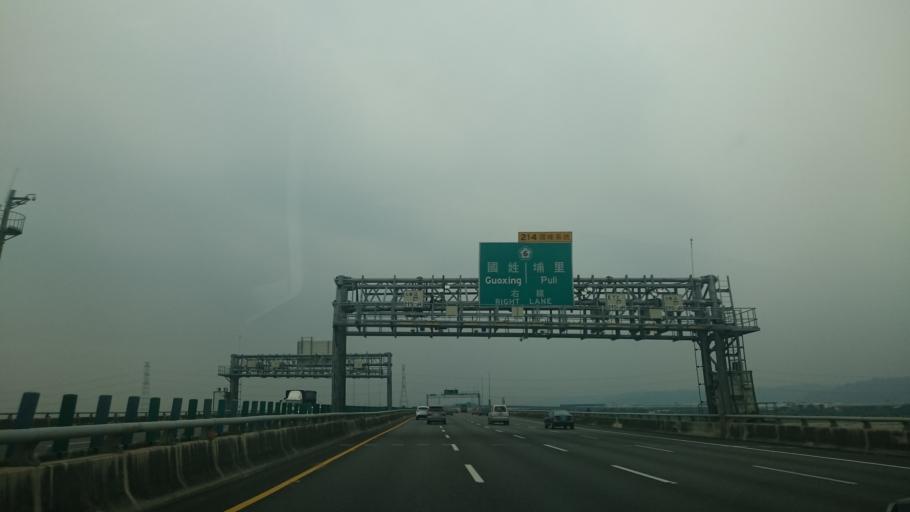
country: TW
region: Taiwan
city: Zhongxing New Village
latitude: 24.0191
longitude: 120.6630
